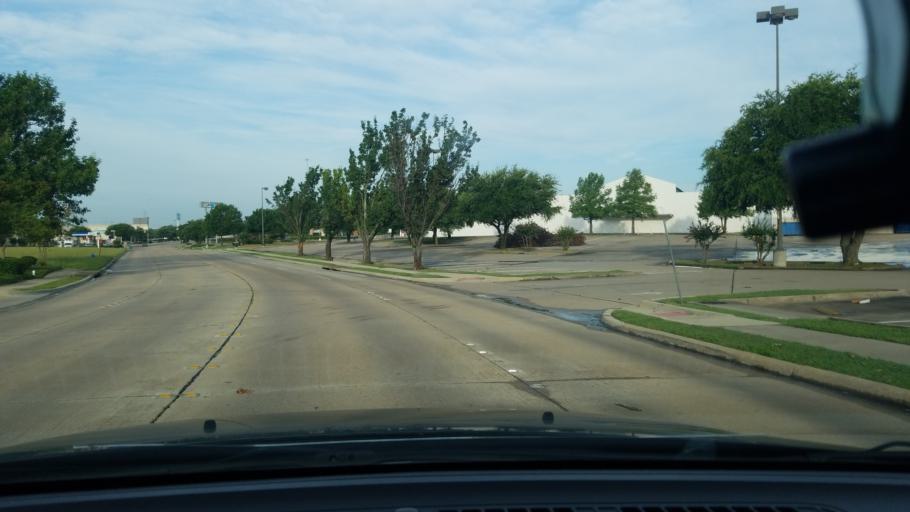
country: US
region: Texas
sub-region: Dallas County
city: Mesquite
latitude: 32.8047
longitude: -96.6217
